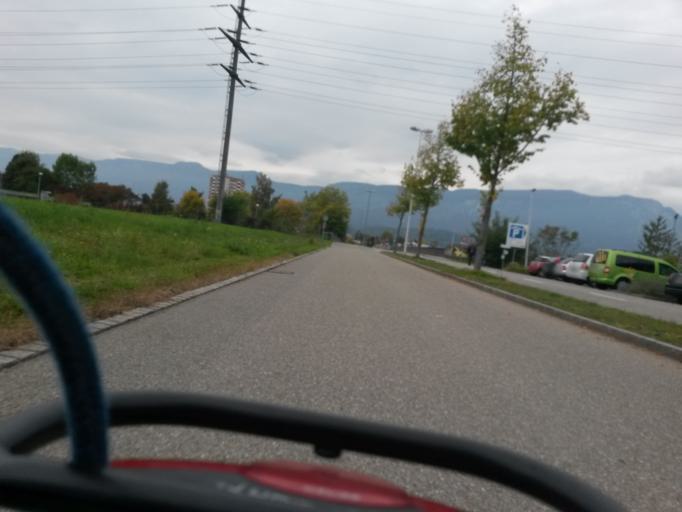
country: CH
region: Solothurn
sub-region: Bezirk Wasseramt
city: Zuchwil
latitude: 47.2012
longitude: 7.5687
